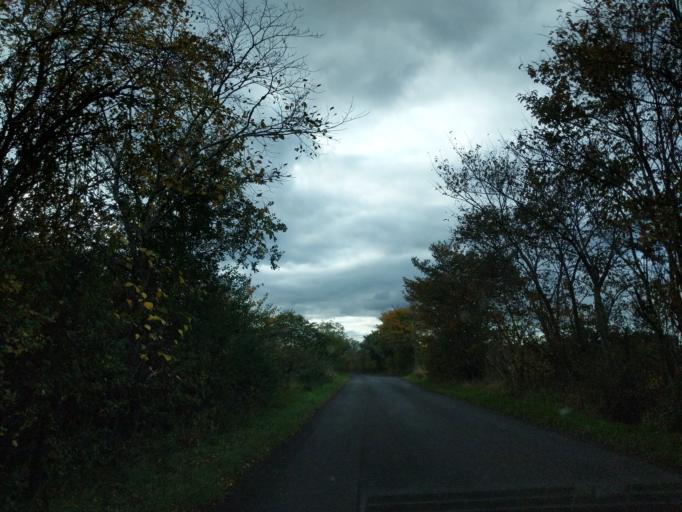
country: GB
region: Scotland
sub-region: East Lothian
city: Haddington
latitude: 55.9373
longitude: -2.7417
